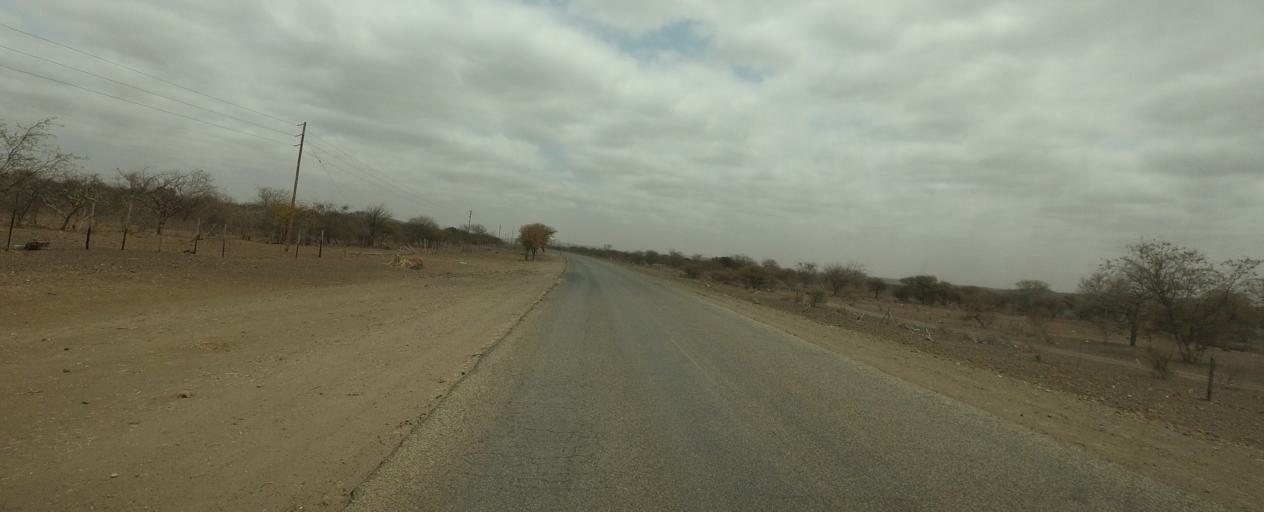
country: ZA
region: Limpopo
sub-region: Vhembe District Municipality
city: Mutale
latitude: -22.4013
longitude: 30.5834
